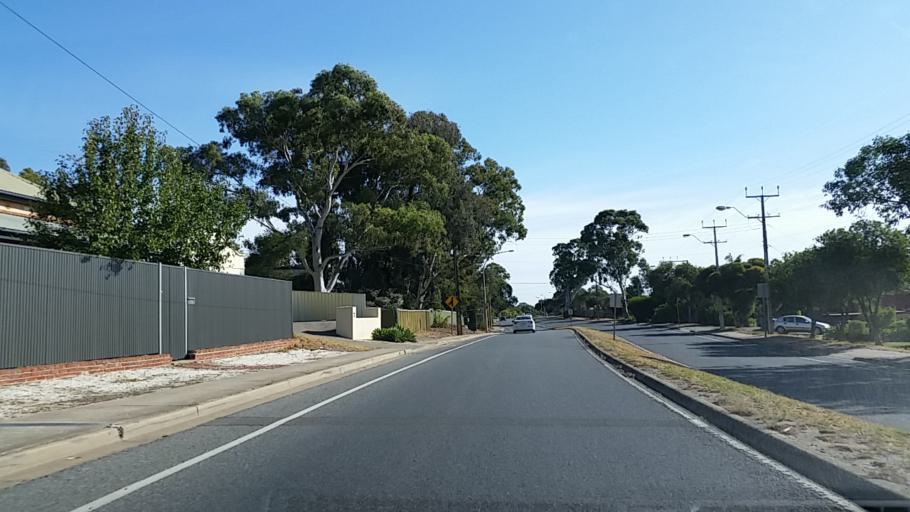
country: AU
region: South Australia
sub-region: Tea Tree Gully
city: Hope Valley
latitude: -34.8500
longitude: 138.7143
